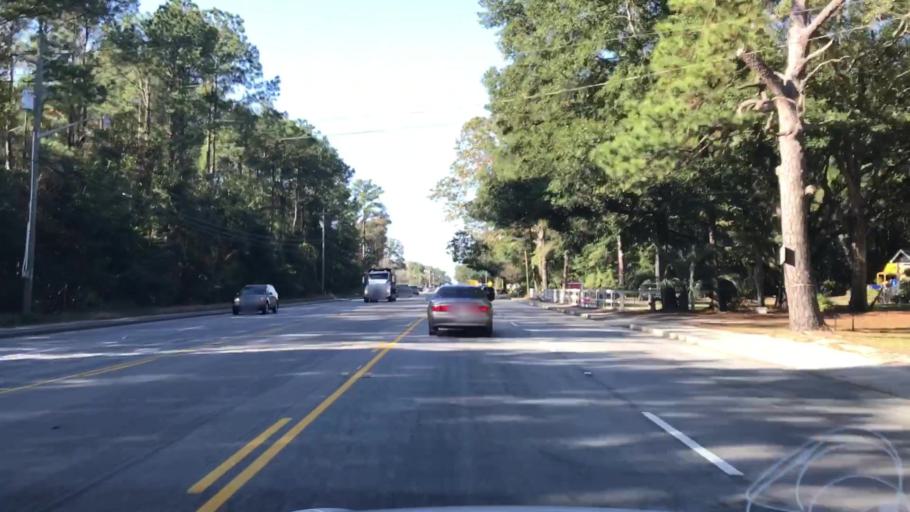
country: US
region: South Carolina
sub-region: Charleston County
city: Ravenel
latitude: 32.7808
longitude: -80.2243
